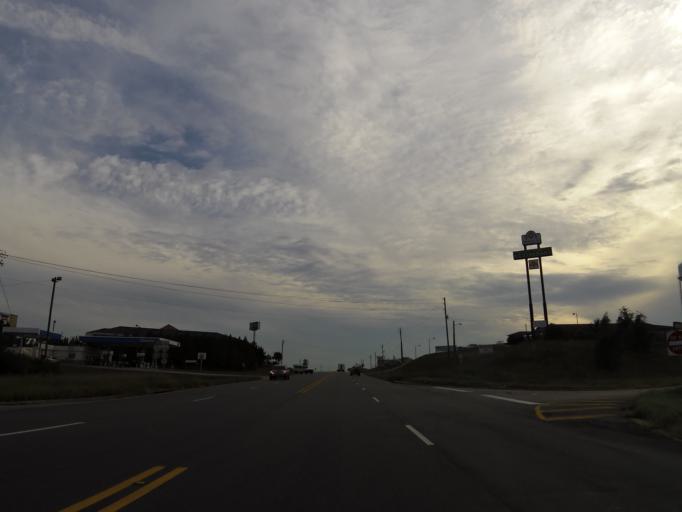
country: US
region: Alabama
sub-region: Escambia County
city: Atmore
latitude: 31.1100
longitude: -87.4744
